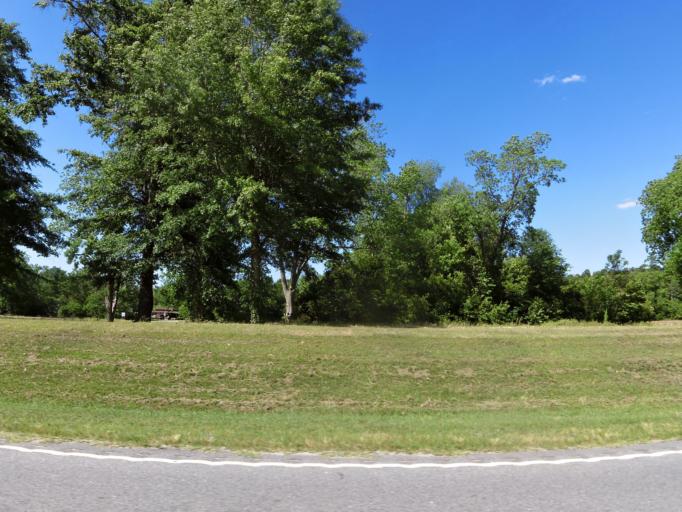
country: US
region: South Carolina
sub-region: Barnwell County
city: Williston
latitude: 33.3801
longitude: -81.3774
